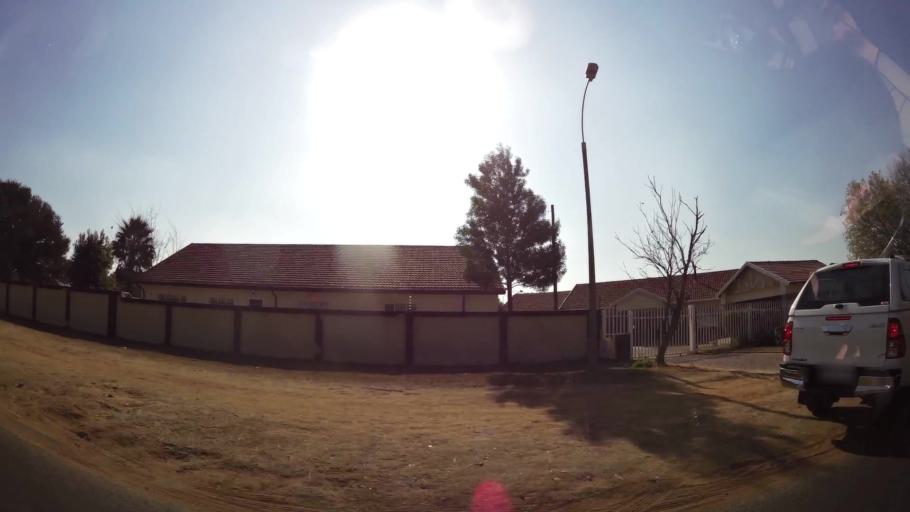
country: ZA
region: Gauteng
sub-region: West Rand District Municipality
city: Randfontein
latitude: -26.1861
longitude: 27.6817
